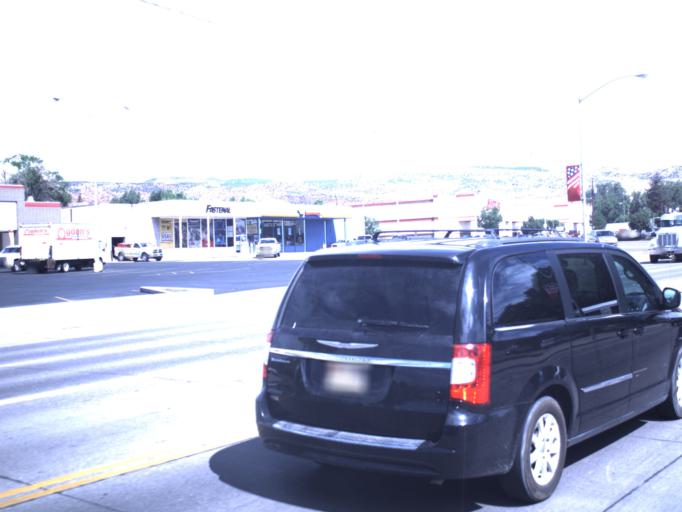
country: US
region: Utah
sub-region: Sevier County
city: Richfield
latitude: 38.7627
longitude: -112.0847
